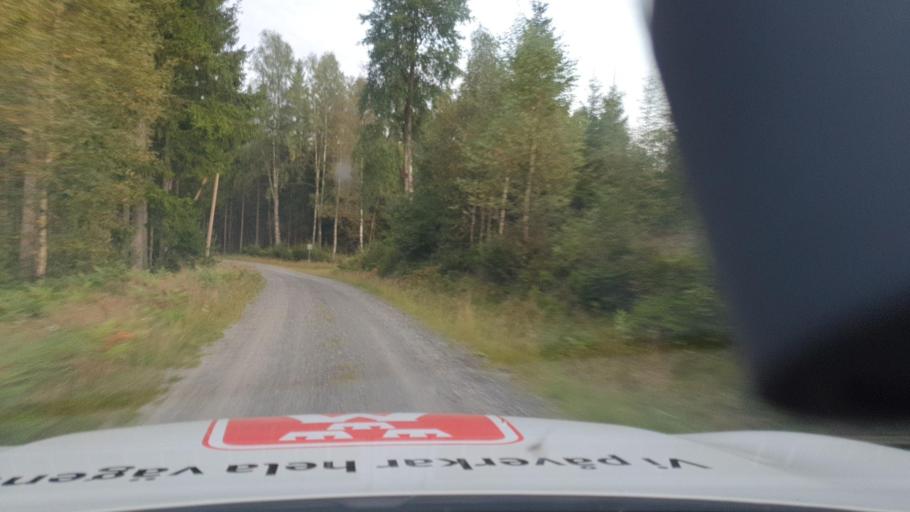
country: SE
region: Vaestra Goetaland
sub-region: Harryda Kommun
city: Hindas
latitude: 57.6909
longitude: 12.4665
